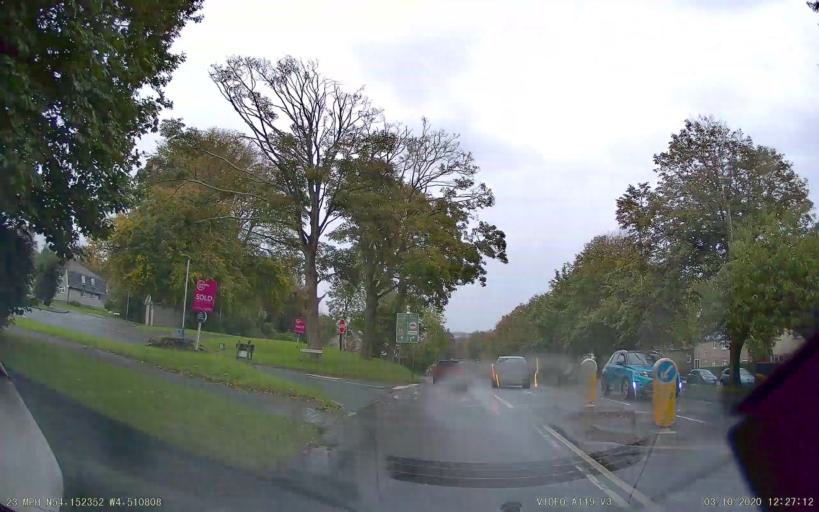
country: IM
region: Douglas
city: Douglas
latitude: 54.1924
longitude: -4.5108
